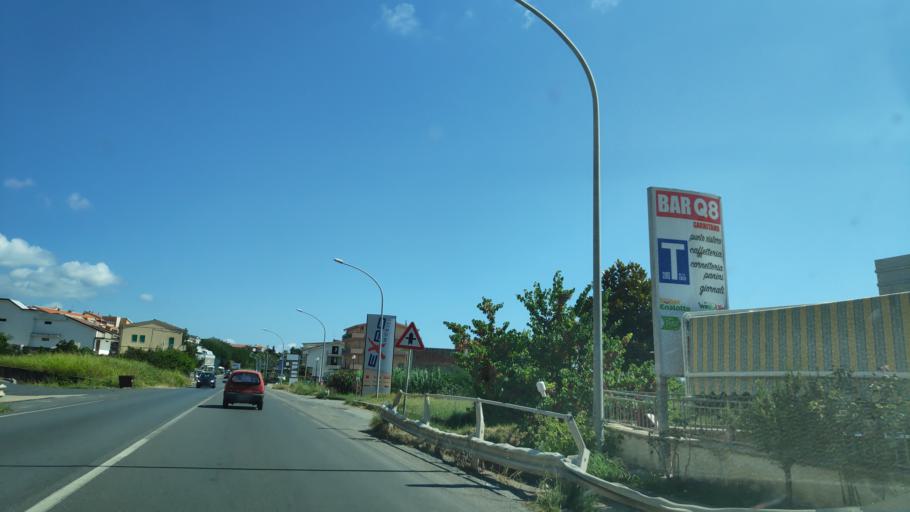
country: IT
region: Calabria
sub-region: Provincia di Cosenza
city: Campora San Giovanni
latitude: 39.0756
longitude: 16.0902
